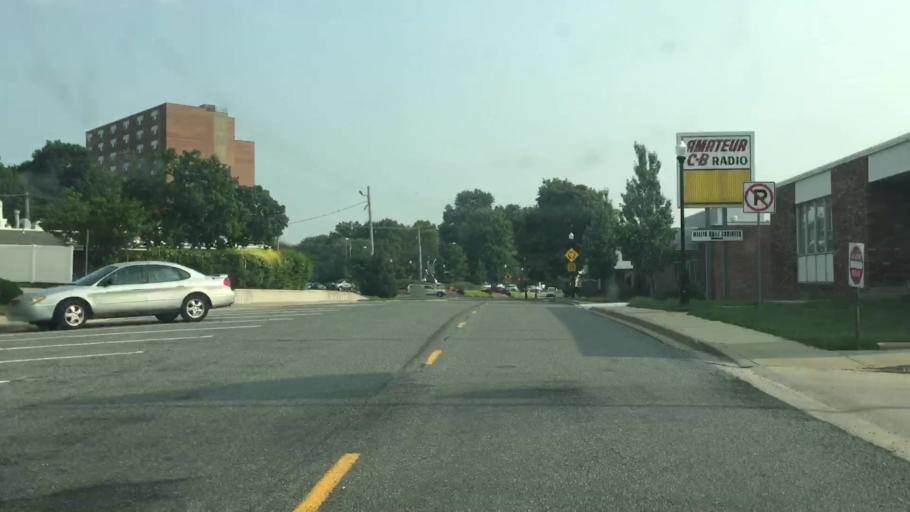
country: US
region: Kansas
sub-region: Johnson County
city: Overland Park
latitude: 38.9836
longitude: -94.6736
